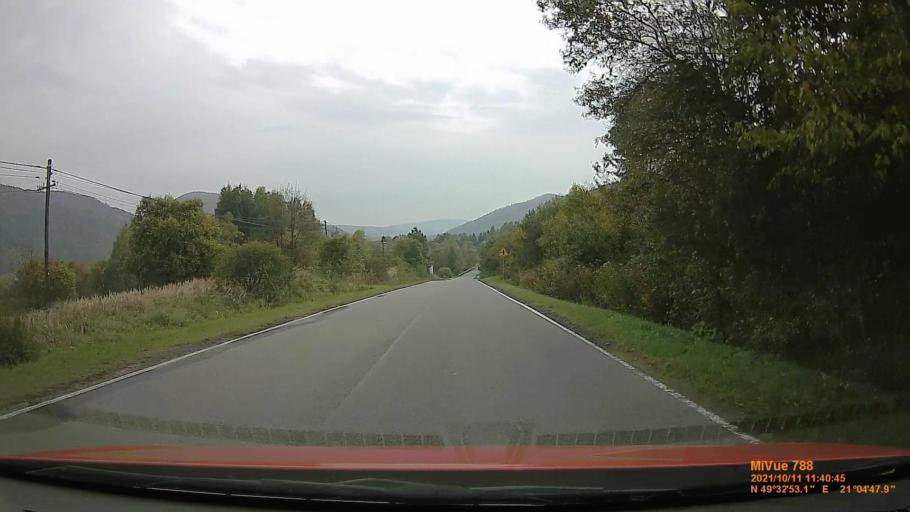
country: PL
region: Lesser Poland Voivodeship
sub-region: Powiat gorlicki
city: Ropa
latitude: 49.5480
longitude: 21.0801
